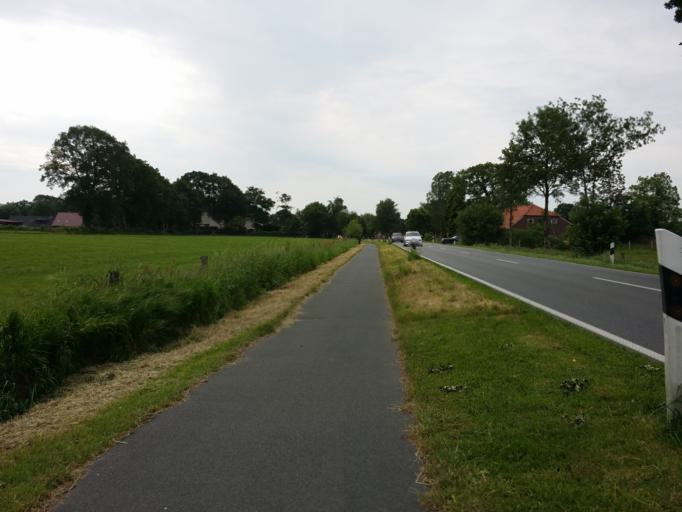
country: DE
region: Lower Saxony
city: Wittmund
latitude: 53.5481
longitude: 7.7829
